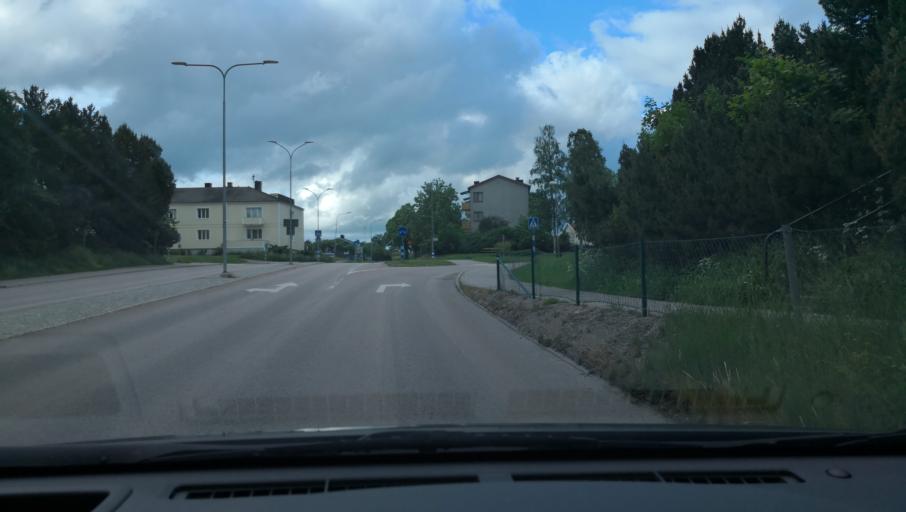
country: SE
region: Vaestmanland
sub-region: Arboga Kommun
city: Arboga
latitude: 59.3969
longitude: 15.8496
